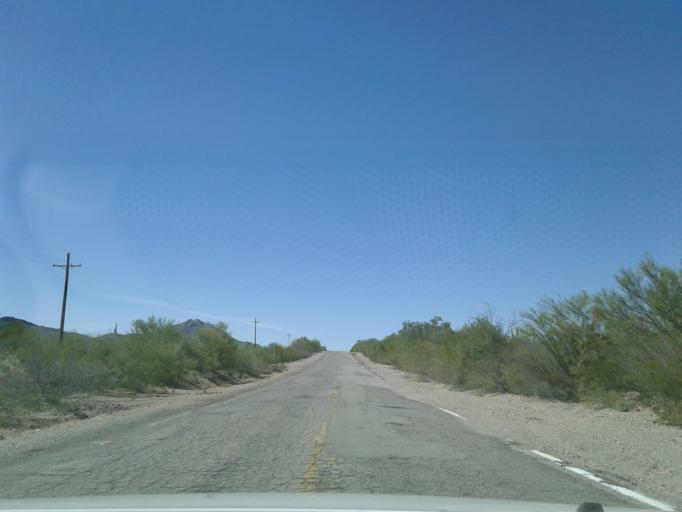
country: US
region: Arizona
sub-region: Pima County
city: Avra Valley
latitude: 32.3713
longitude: -111.4361
